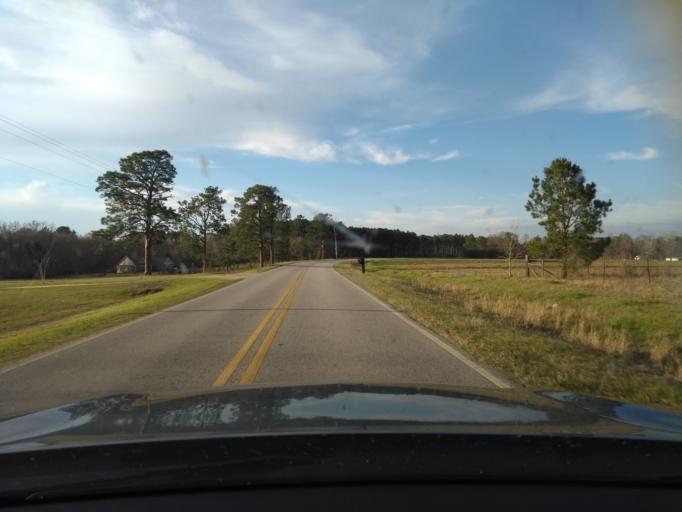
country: US
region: Georgia
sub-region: Bulloch County
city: Brooklet
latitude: 32.3149
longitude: -81.7779
